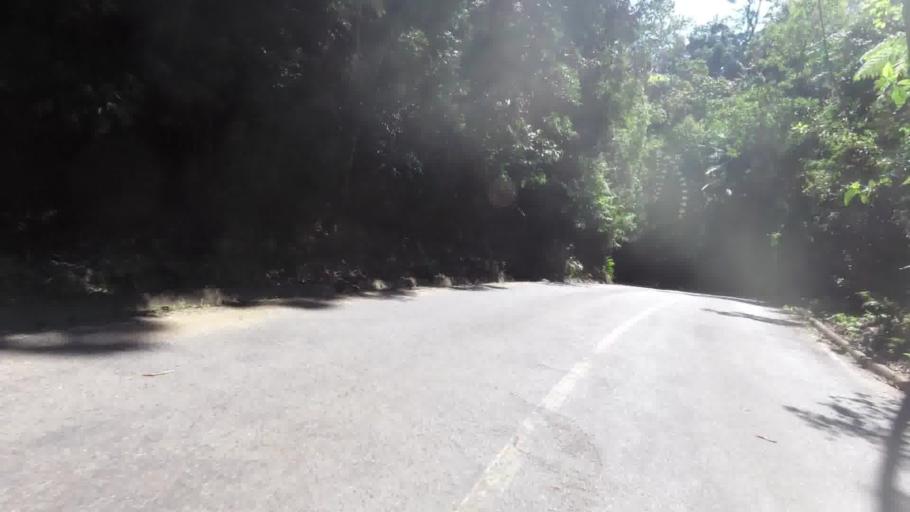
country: BR
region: Espirito Santo
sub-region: Marechal Floriano
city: Marechal Floriano
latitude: -20.4537
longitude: -40.9041
